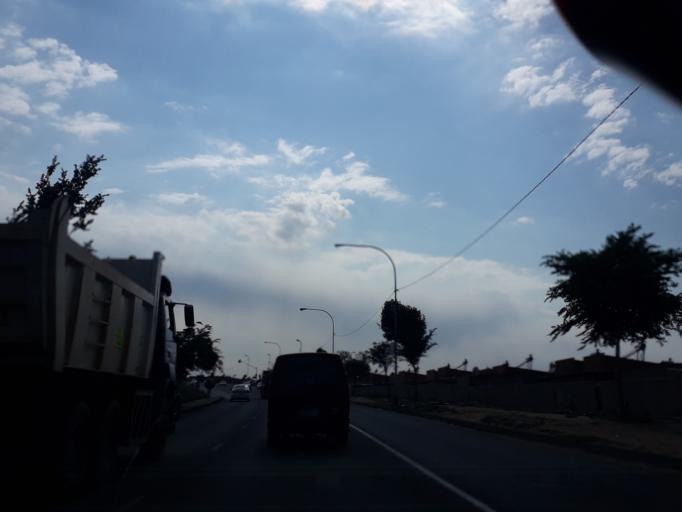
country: ZA
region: Gauteng
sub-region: City of Johannesburg Metropolitan Municipality
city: Modderfontein
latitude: -26.1063
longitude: 28.1193
